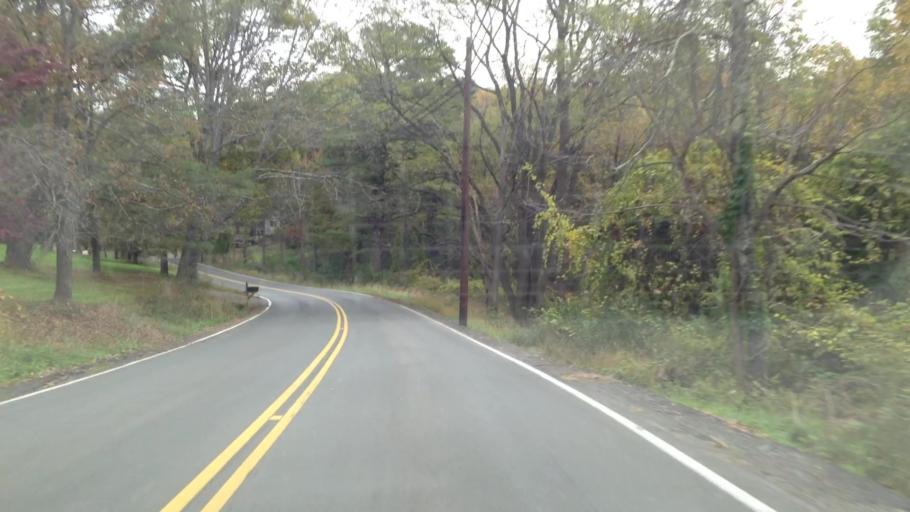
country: US
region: New York
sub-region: Dutchess County
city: Hyde Park
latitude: 41.8265
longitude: -73.9921
